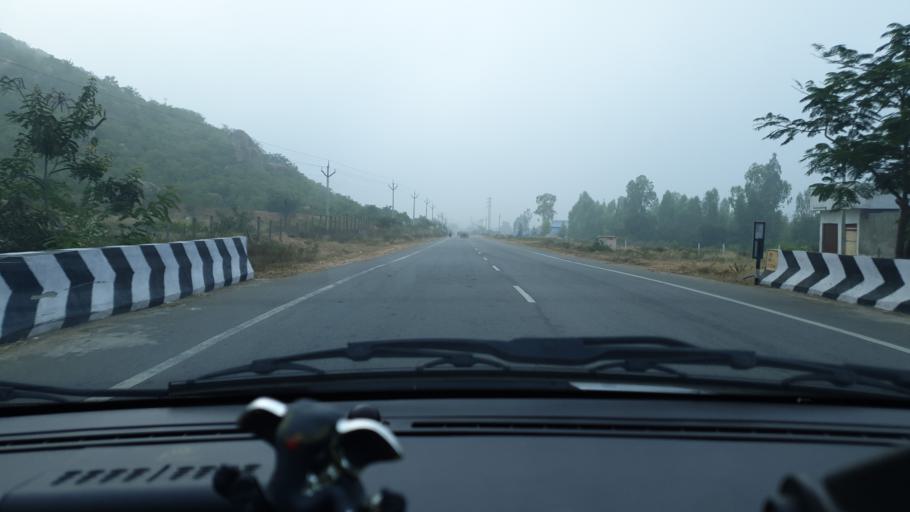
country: IN
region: Telangana
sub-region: Mahbubnagar
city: Farrukhnagar
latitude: 16.9090
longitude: 78.5284
